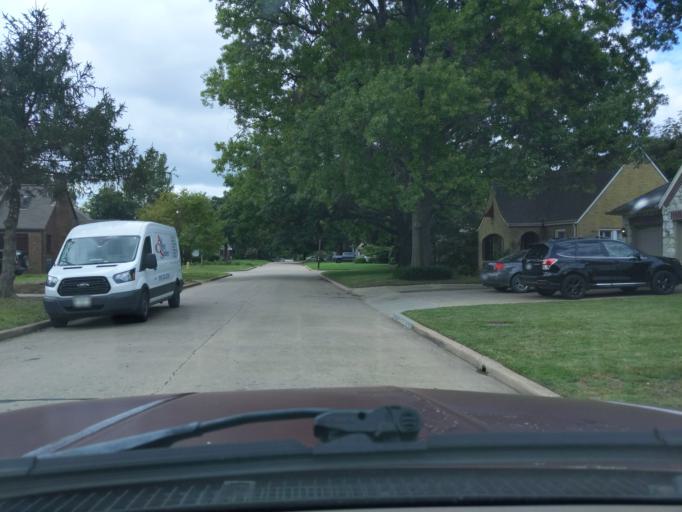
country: US
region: Oklahoma
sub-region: Tulsa County
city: Tulsa
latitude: 36.1107
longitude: -95.9796
